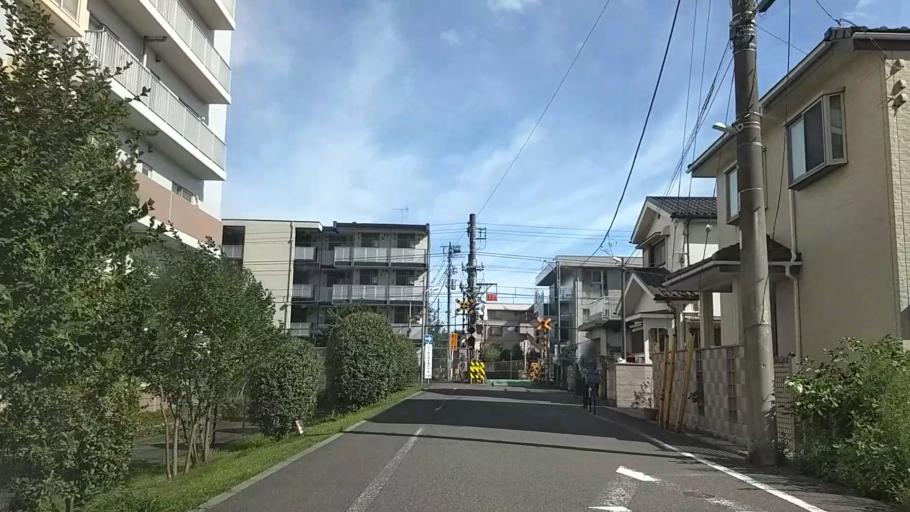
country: JP
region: Tokyo
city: Hachioji
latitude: 35.6528
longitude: 139.3044
